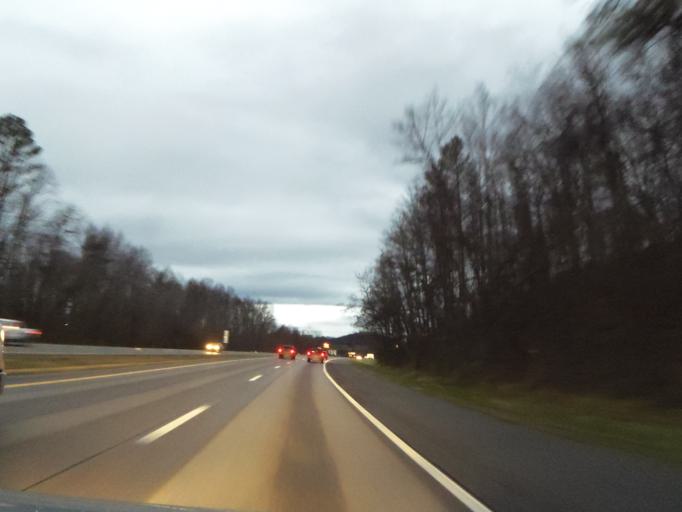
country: US
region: Tennessee
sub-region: Washington County
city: Oak Grove
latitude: 36.3719
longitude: -82.4212
